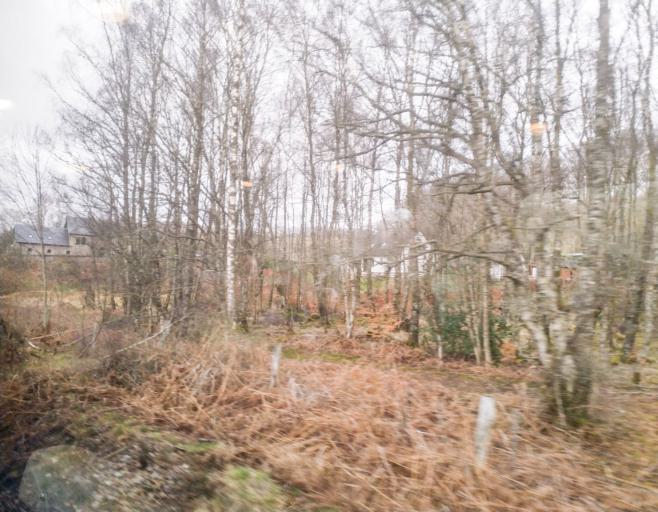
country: GB
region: Scotland
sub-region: Highland
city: Spean Bridge
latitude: 56.8881
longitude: -4.8350
